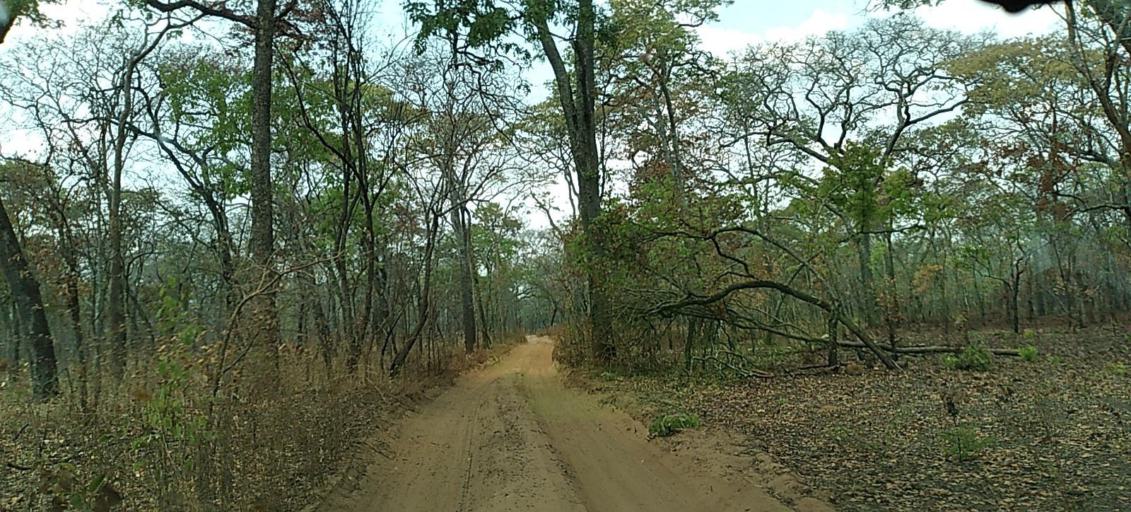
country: ZM
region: North-Western
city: Kabompo
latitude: -13.6147
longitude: 24.3715
